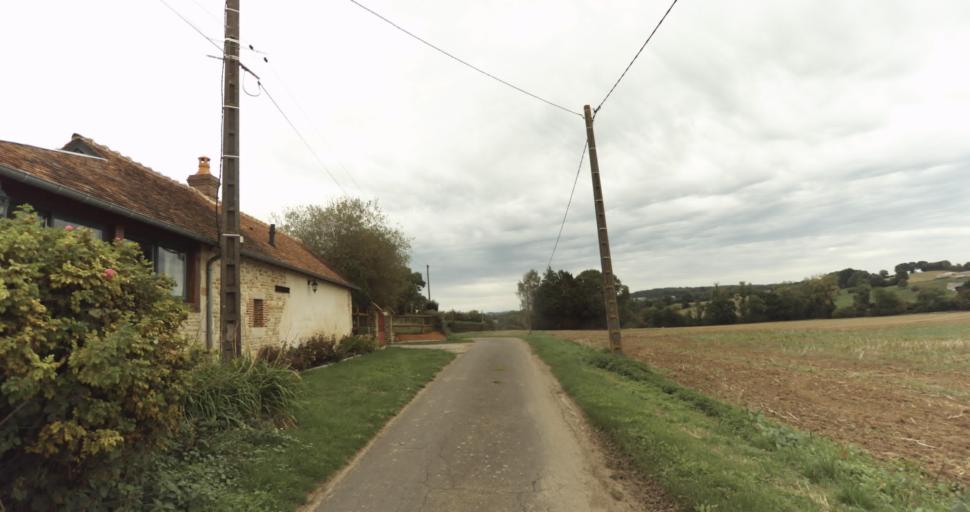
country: FR
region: Lower Normandy
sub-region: Departement de l'Orne
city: Gace
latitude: 48.6858
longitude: 0.2700
